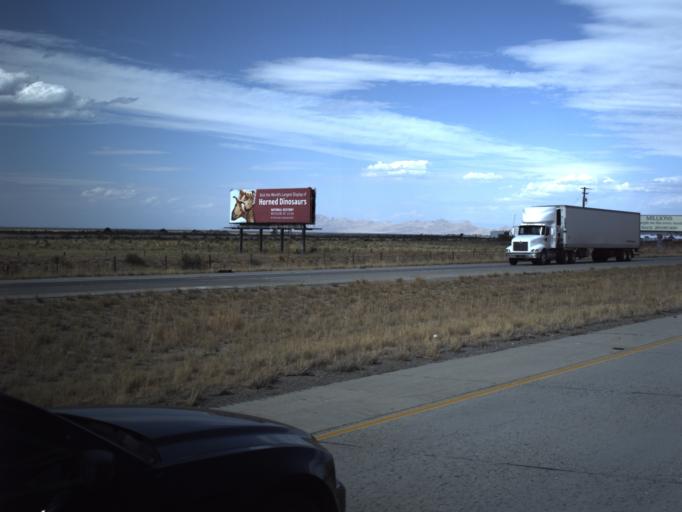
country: US
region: Utah
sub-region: Tooele County
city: Stansbury park
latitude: 40.6796
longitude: -112.2795
